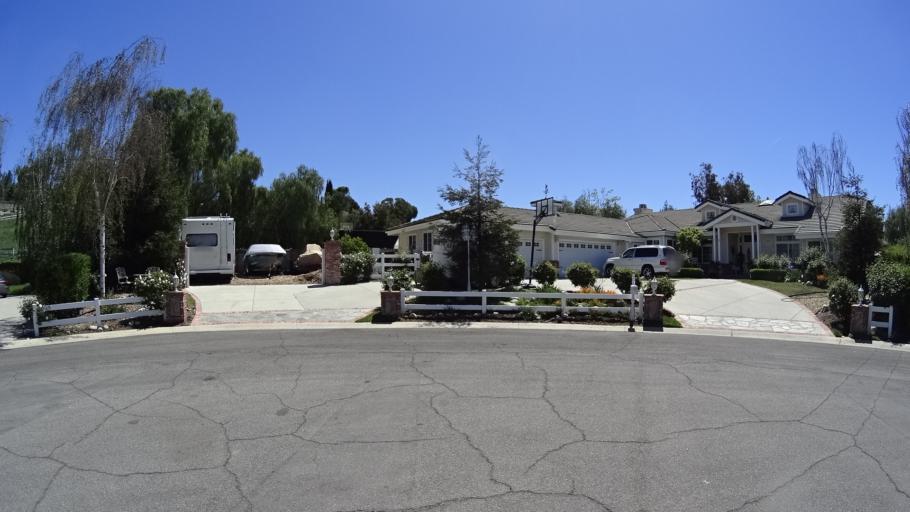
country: US
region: California
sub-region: Ventura County
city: Thousand Oaks
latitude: 34.1870
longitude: -118.8532
